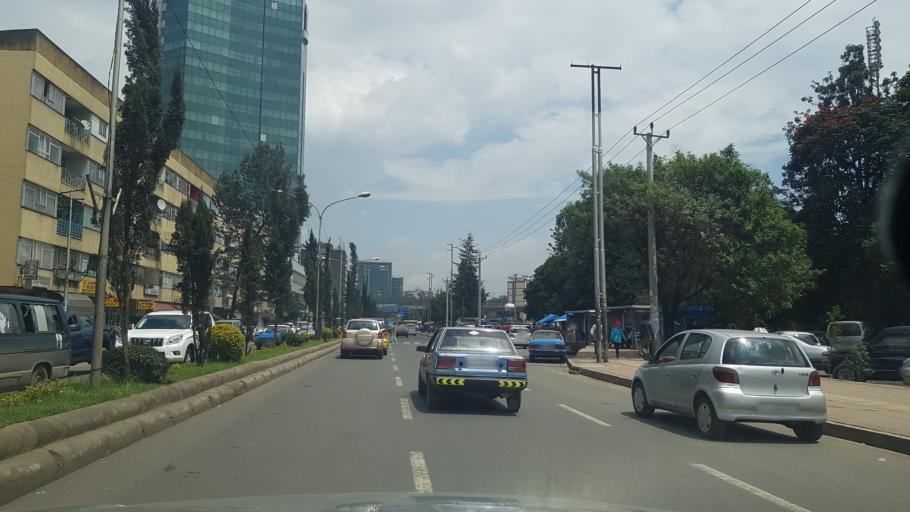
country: ET
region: Adis Abeba
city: Addis Ababa
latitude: 9.0142
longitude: 38.7572
